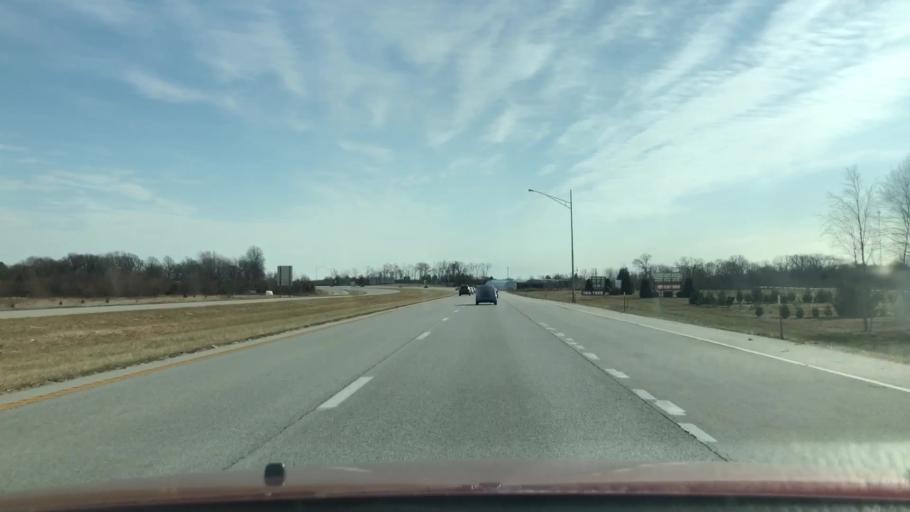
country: US
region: Missouri
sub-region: Webster County
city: Rogersville
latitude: 37.1111
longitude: -93.0694
